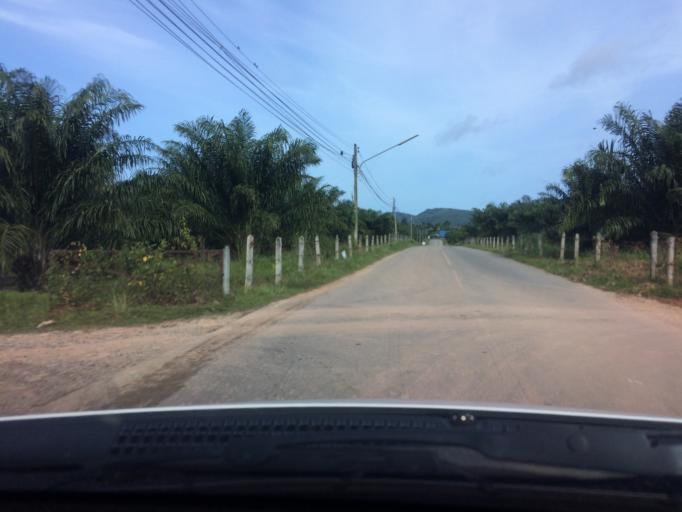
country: TH
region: Phuket
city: Thalang
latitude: 8.0434
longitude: 98.3331
